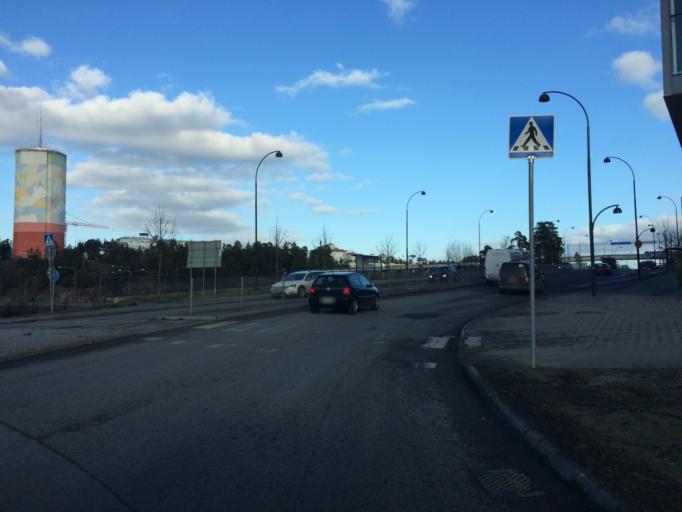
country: SE
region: Stockholm
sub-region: Nacka Kommun
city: Nacka
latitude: 59.3108
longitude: 18.1626
